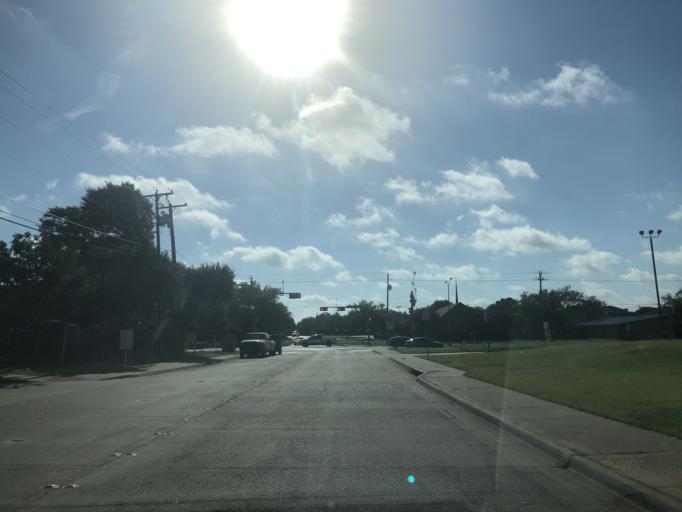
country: US
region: Texas
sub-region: Dallas County
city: Duncanville
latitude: 32.6587
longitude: -96.9267
